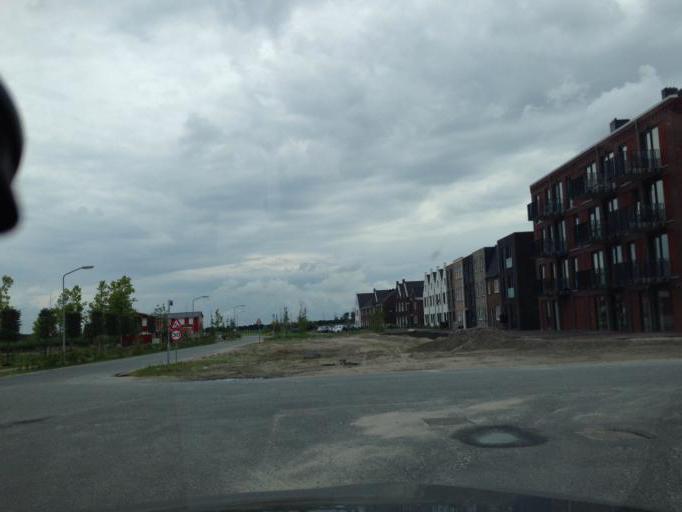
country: NL
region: Flevoland
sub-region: Gemeente Almere
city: Almere Stad
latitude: 52.3573
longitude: 5.2839
